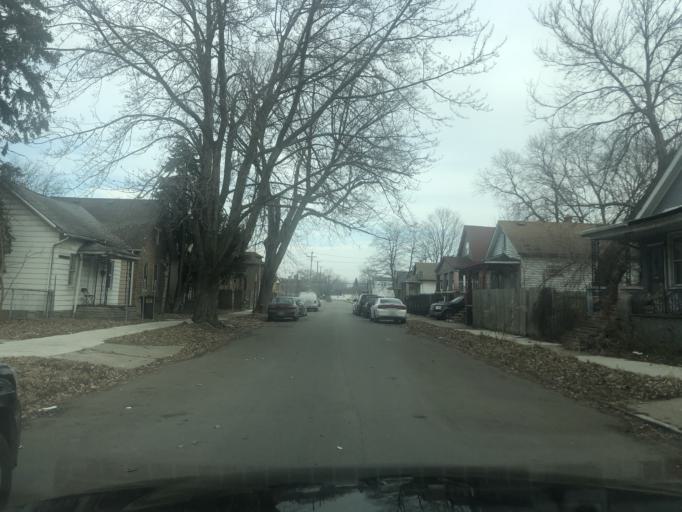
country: US
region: Michigan
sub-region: Wayne County
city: Detroit
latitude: 42.3230
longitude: -83.1017
